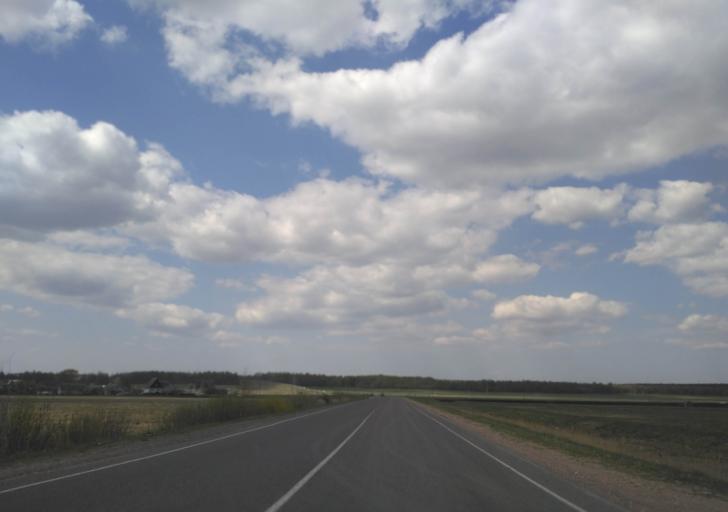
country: BY
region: Minsk
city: Vilyeyka
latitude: 54.5192
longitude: 26.9749
